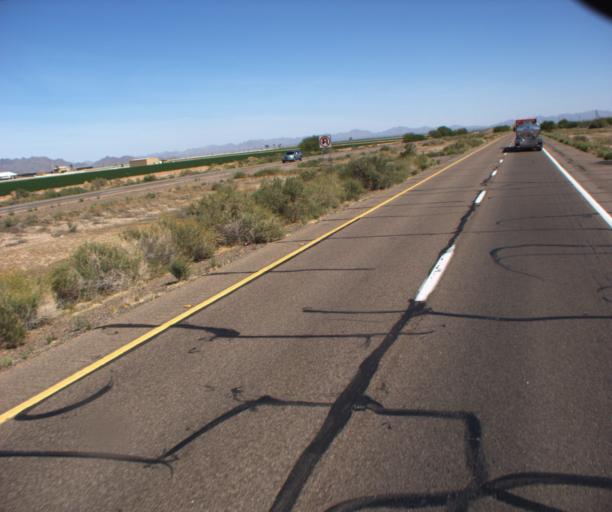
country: US
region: Arizona
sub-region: Maricopa County
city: Gila Bend
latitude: 32.9306
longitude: -112.8156
